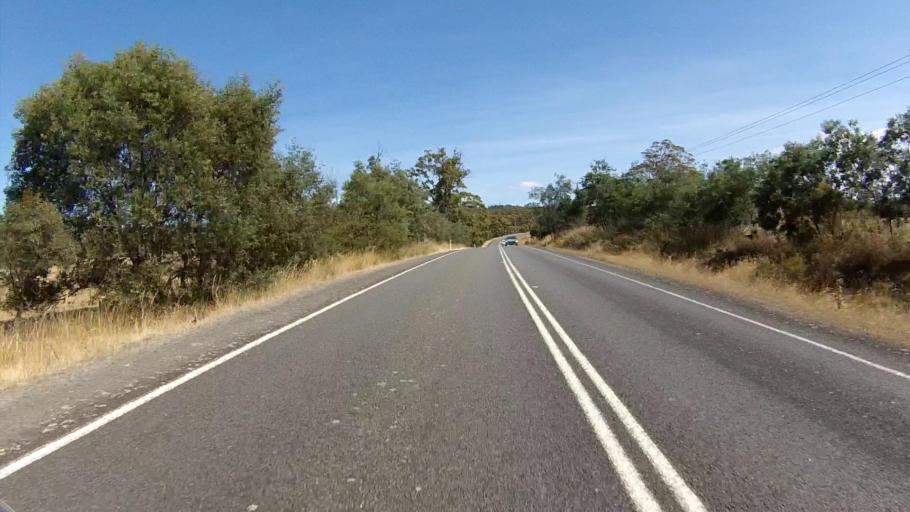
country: AU
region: Tasmania
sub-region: Sorell
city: Sorell
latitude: -42.5788
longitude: 147.8165
